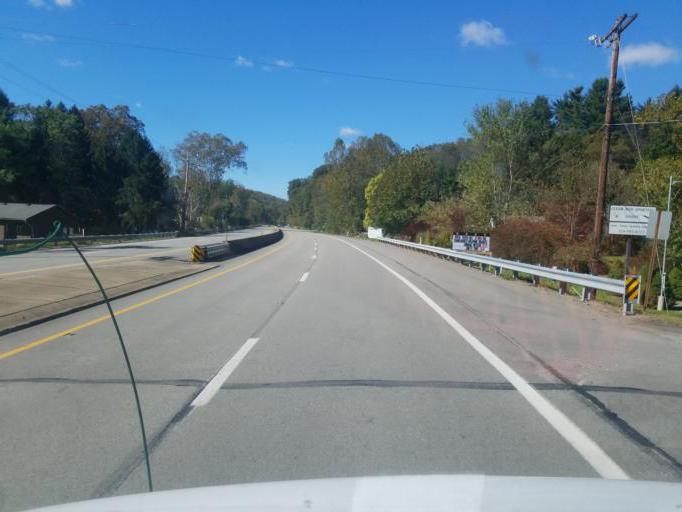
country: US
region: Pennsylvania
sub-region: Westmoreland County
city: Ligonier
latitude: 40.2379
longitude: -79.2314
